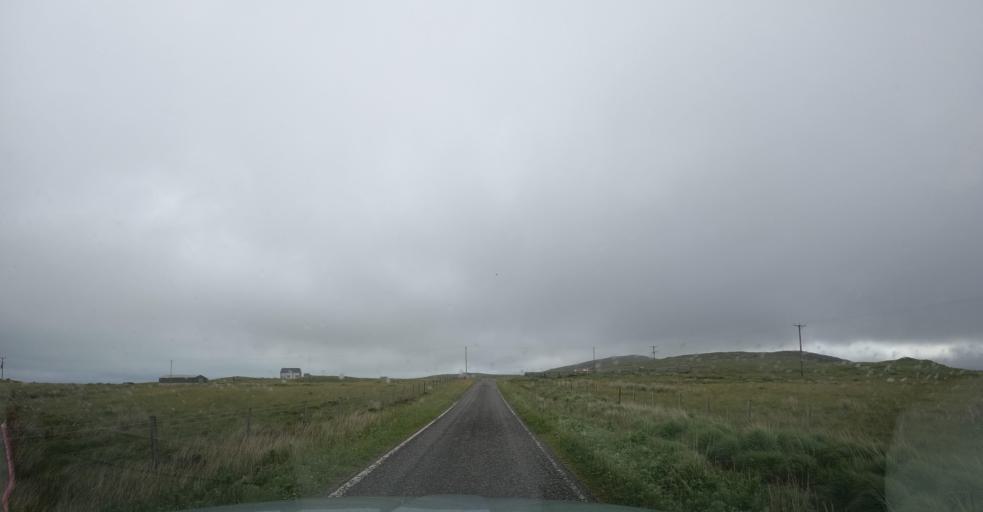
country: GB
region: Scotland
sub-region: Eilean Siar
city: Isle of North Uist
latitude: 57.6565
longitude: -7.2415
